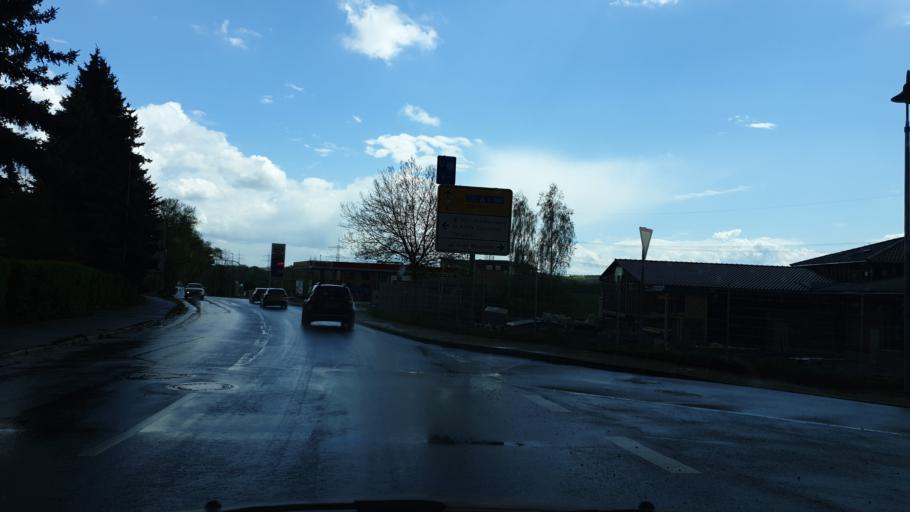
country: DE
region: Saxony
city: Limbach-Oberfrohna
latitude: 50.8135
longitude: 12.8100
